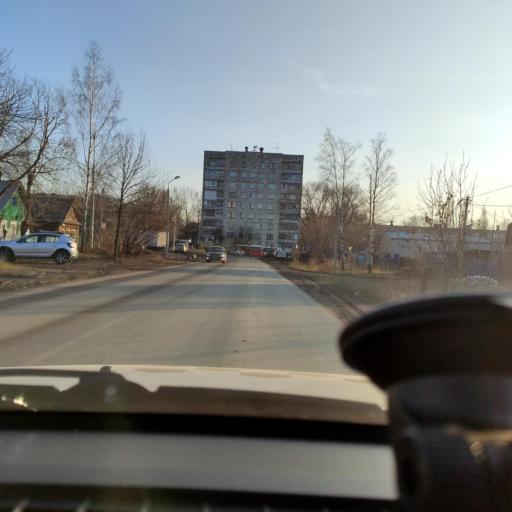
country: RU
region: Perm
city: Perm
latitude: 57.9826
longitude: 56.2940
